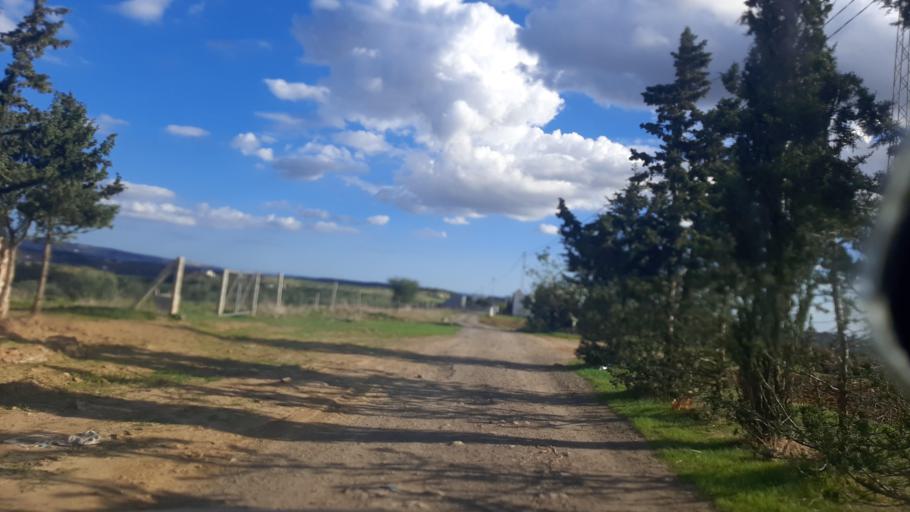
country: TN
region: Nabul
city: Bu `Urqub
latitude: 36.4679
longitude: 10.4792
